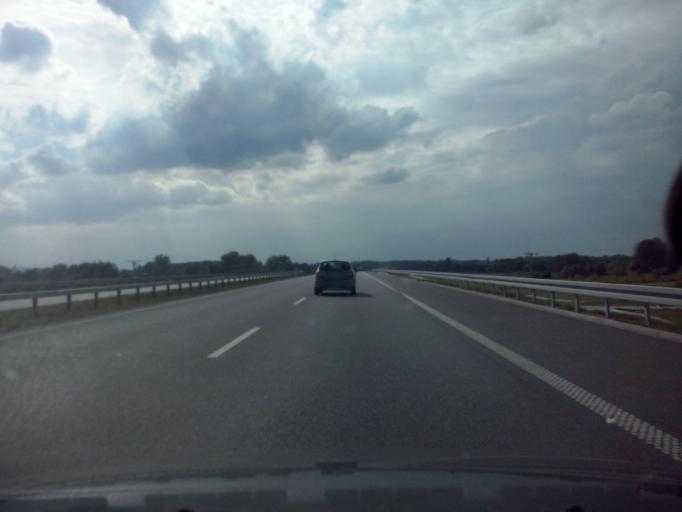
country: PL
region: Lesser Poland Voivodeship
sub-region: Powiat brzeski
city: Maszkienice
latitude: 50.0050
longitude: 20.7199
